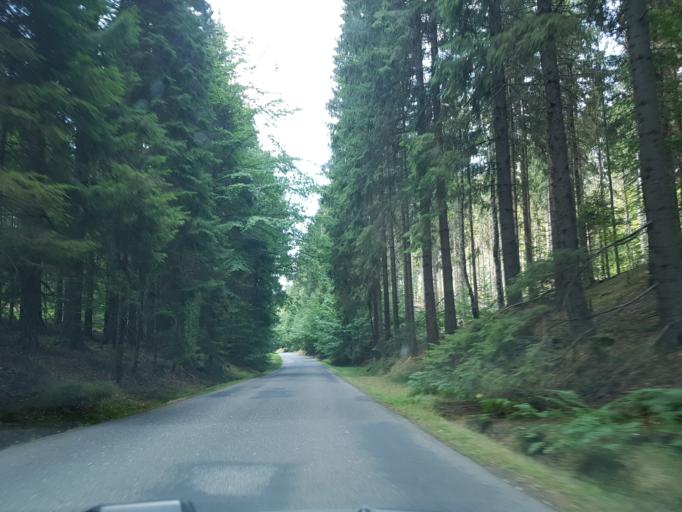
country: CZ
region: Ustecky
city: Mikulasovice
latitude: 50.8740
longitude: 14.3126
